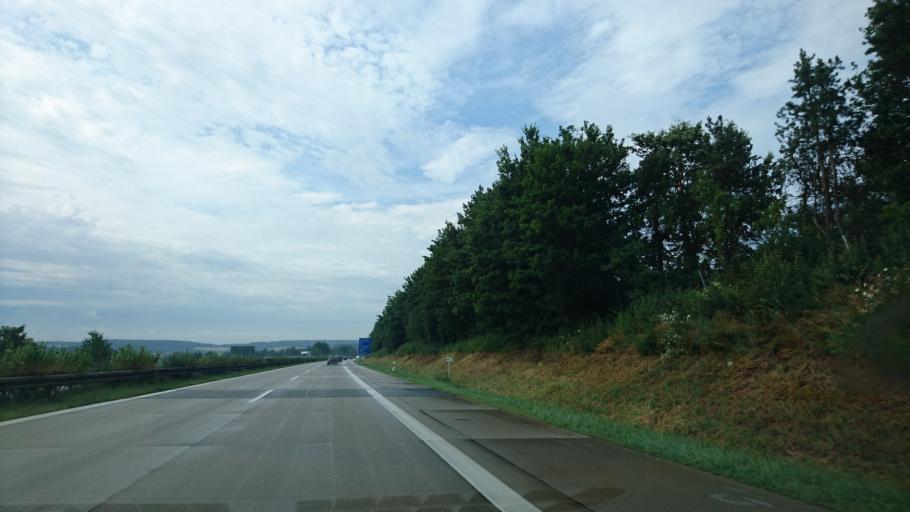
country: DE
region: Bavaria
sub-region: Lower Bavaria
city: Bad Abbach
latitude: 48.9414
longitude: 12.0915
